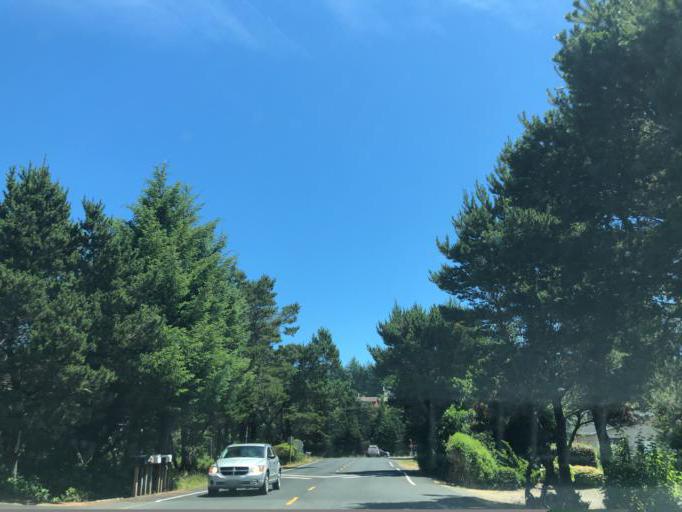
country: US
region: Oregon
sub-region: Lincoln County
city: Waldport
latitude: 44.4415
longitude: -124.0767
